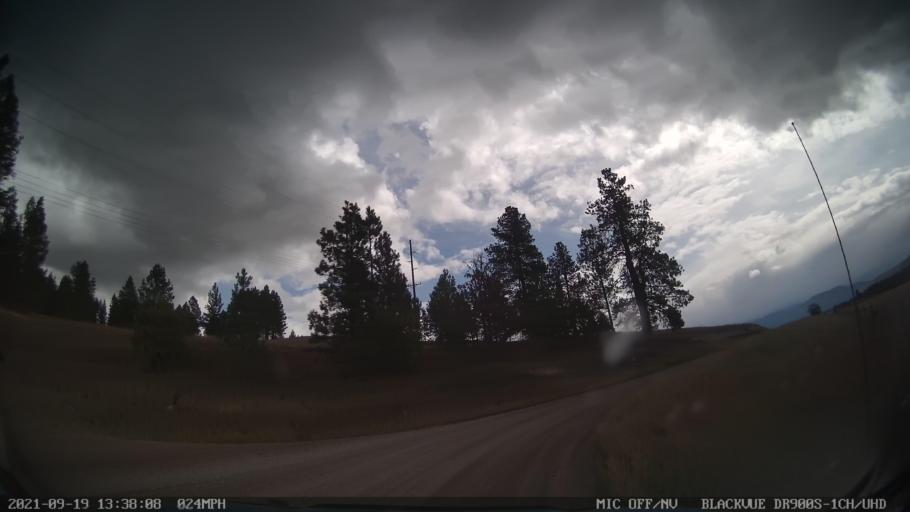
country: US
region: Montana
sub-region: Missoula County
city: Seeley Lake
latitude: 47.1066
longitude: -113.2727
